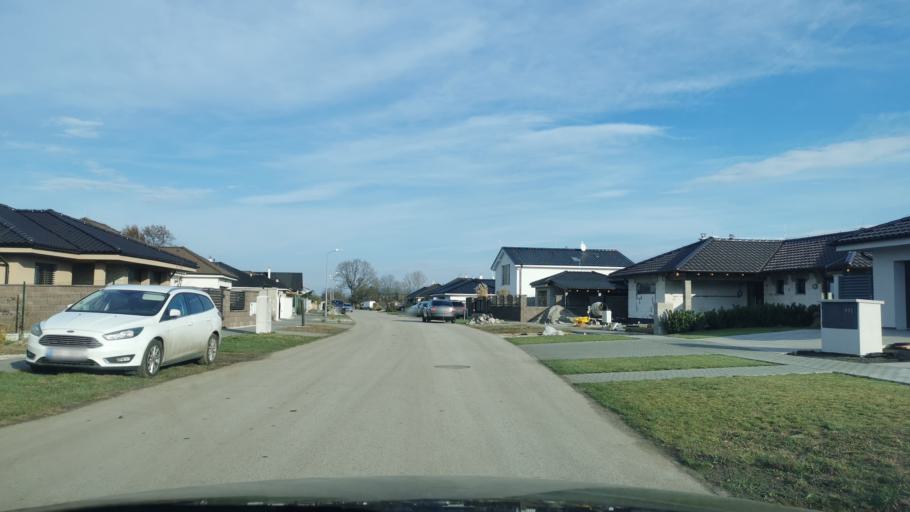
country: SK
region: Trnavsky
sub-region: Okres Skalica
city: Holic
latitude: 48.7875
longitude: 17.1221
